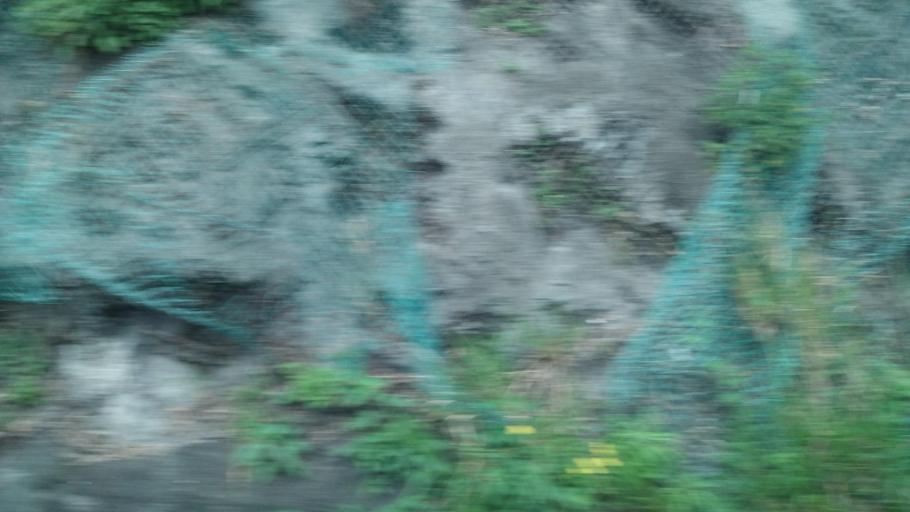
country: TW
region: Taiwan
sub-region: Hualien
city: Hualian
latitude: 24.2185
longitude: 121.6922
